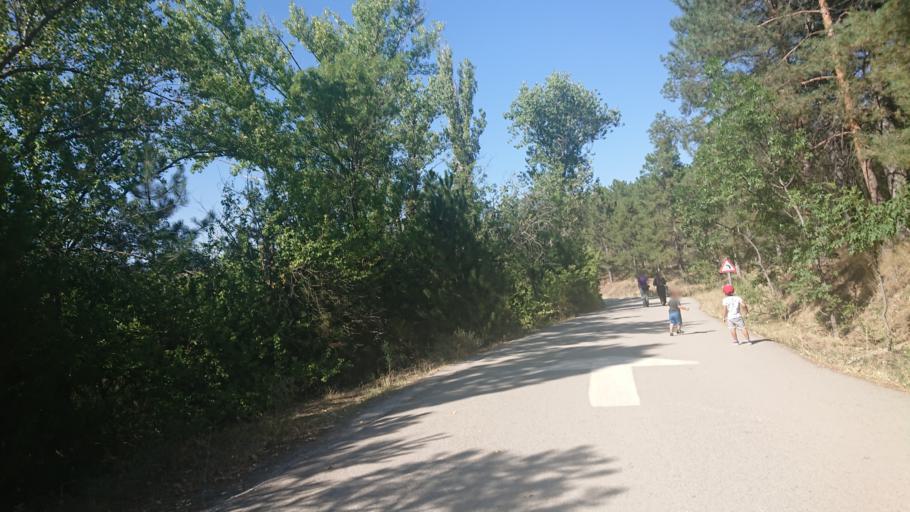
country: TR
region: Ankara
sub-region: Goelbasi
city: Golbasi
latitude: 39.8154
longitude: 32.8211
